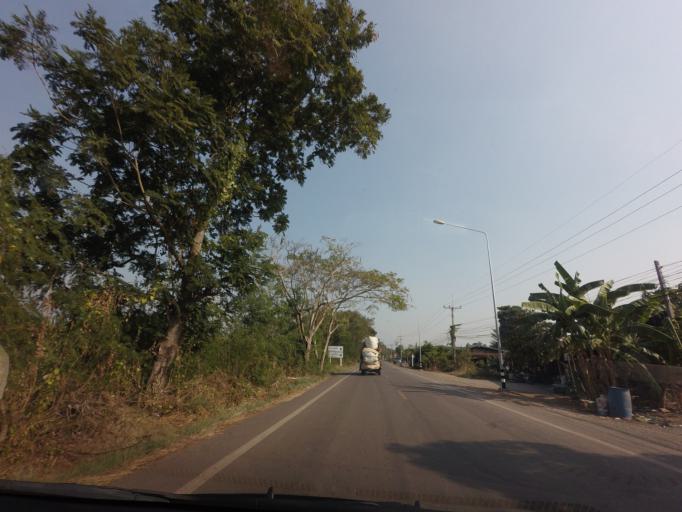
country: TH
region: Chachoengsao
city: Khlong Khuean
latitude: 13.8182
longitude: 101.1831
